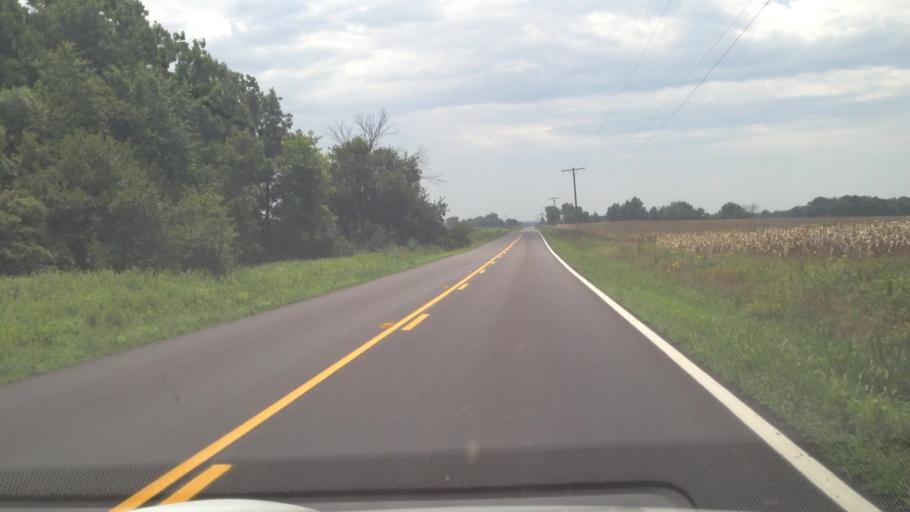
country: US
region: Kansas
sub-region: Crawford County
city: Girard
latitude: 37.6348
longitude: -94.9698
